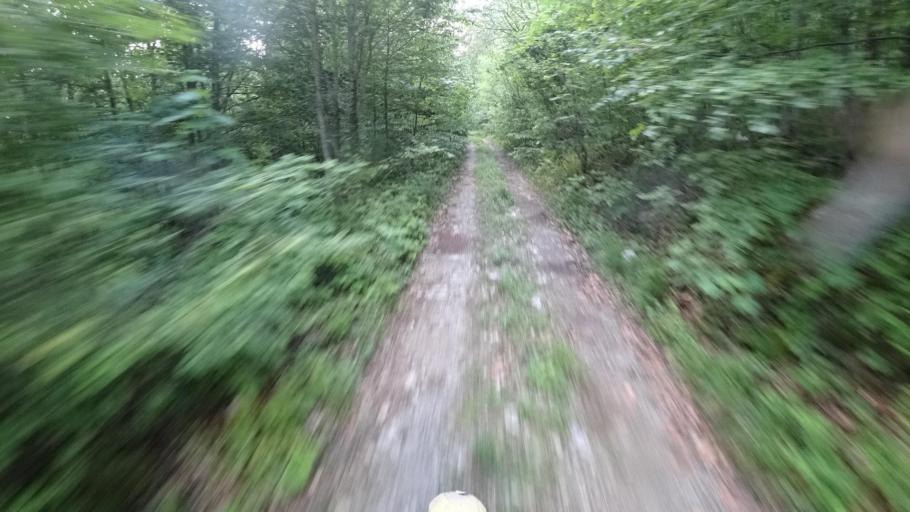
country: BA
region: Federation of Bosnia and Herzegovina
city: Bosanska Krupa
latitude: 44.7656
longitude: 16.3294
